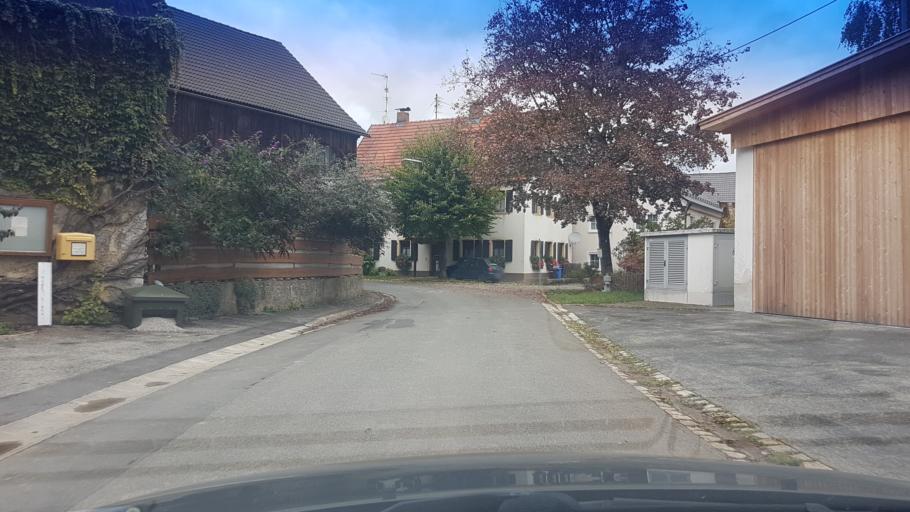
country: DE
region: Bavaria
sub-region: Upper Franconia
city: Wonsees
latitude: 50.0103
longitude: 11.2589
